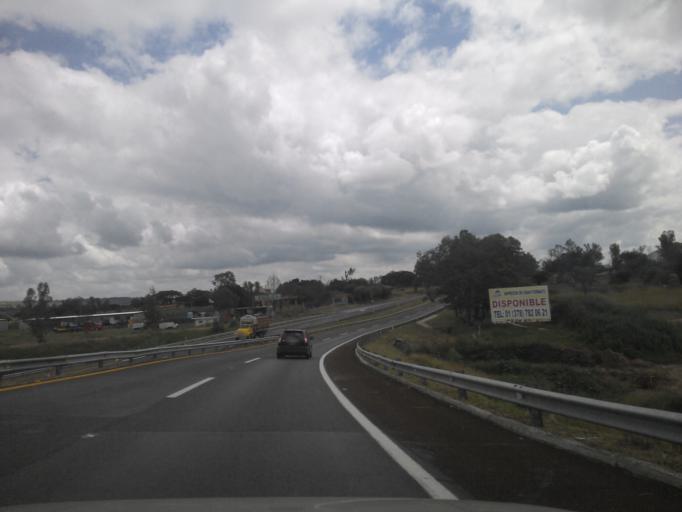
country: MX
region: Jalisco
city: Zapotlanejo
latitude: 20.6142
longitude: -103.0992
